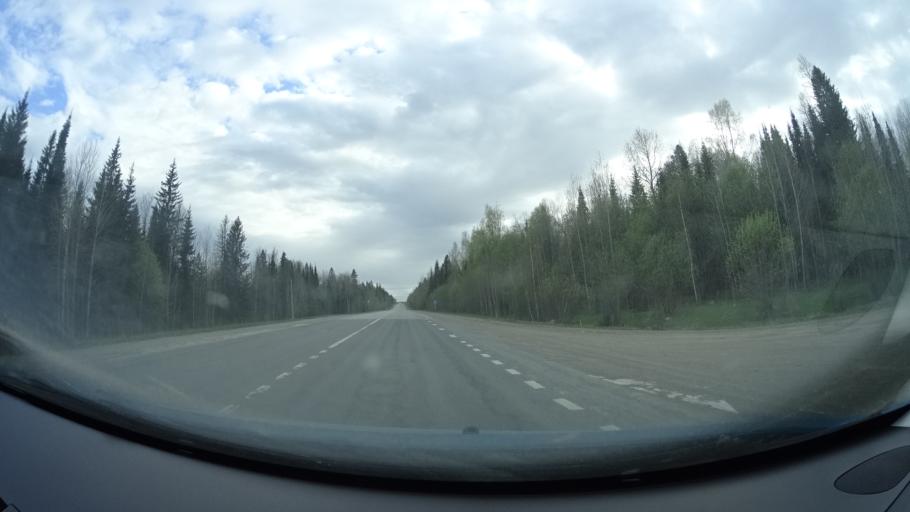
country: RU
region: Perm
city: Kultayevo
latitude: 57.8209
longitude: 55.8027
